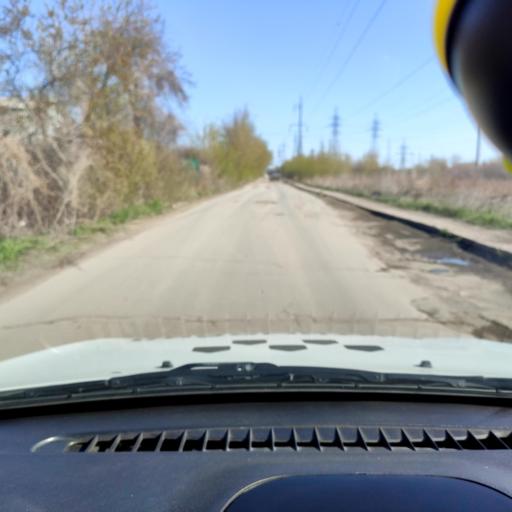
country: RU
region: Samara
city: Tol'yatti
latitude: 53.5847
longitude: 49.2945
